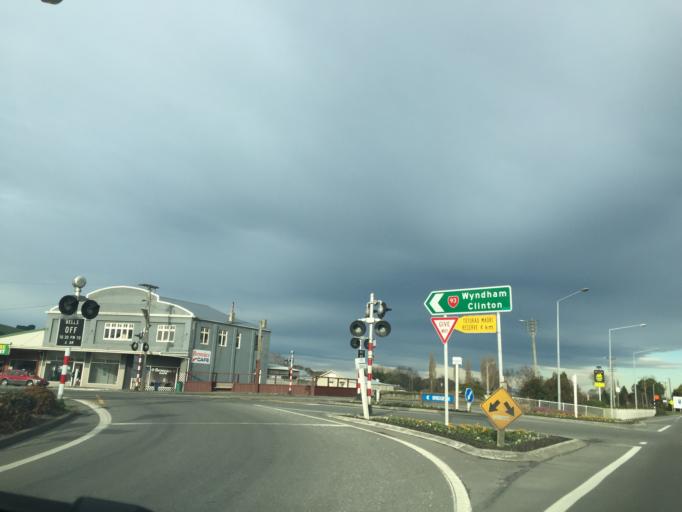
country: NZ
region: Southland
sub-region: Gore District
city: Gore
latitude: -46.1937
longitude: 168.8657
